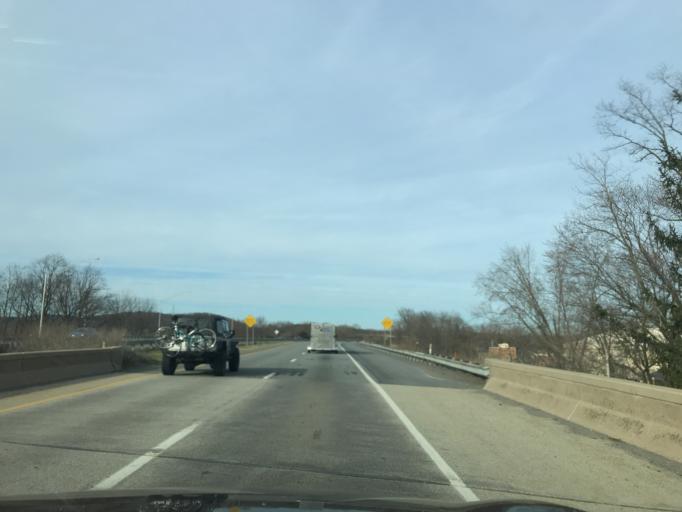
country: US
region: Pennsylvania
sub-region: Lycoming County
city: Duboistown
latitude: 41.2286
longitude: -77.0468
